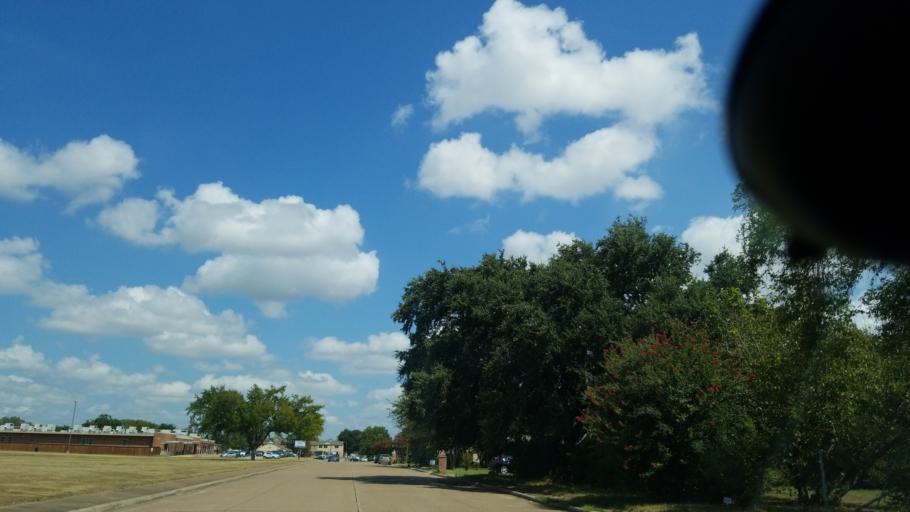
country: US
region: Texas
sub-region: Dallas County
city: Grand Prairie
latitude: 32.7164
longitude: -96.9871
